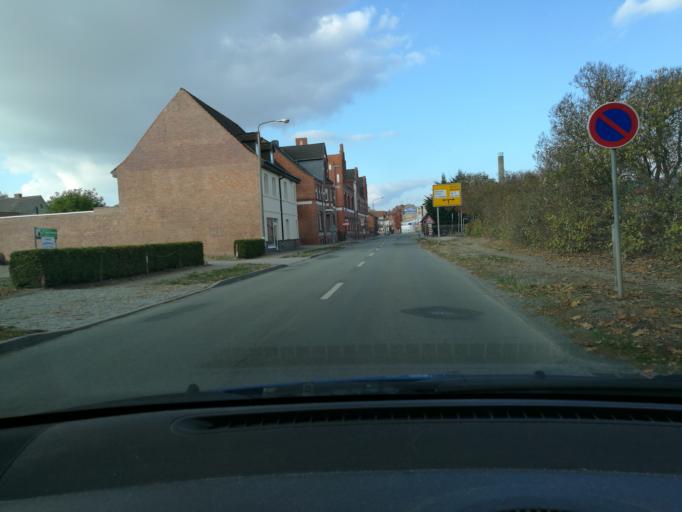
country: DE
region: Saxony-Anhalt
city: Luftkurort Arendsee
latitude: 52.8797
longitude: 11.4900
